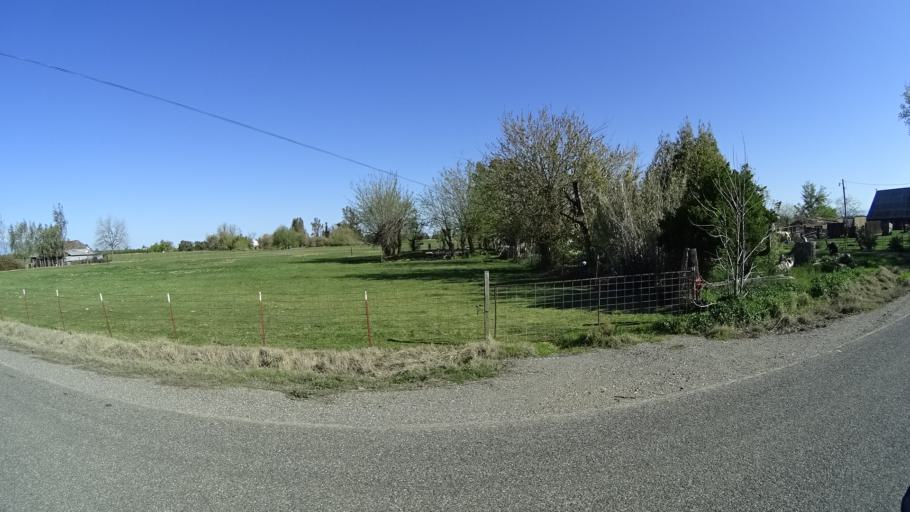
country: US
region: California
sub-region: Glenn County
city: Orland
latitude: 39.7477
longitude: -122.2360
